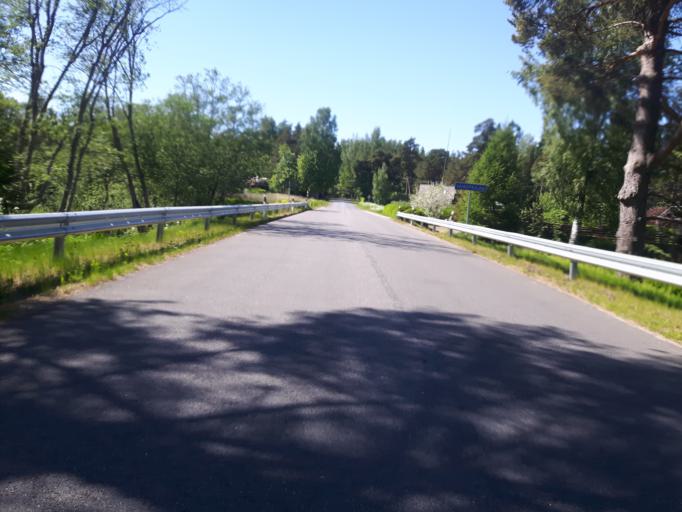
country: EE
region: Laeaene-Virumaa
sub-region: Haljala vald
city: Haljala
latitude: 59.5763
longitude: 26.2743
